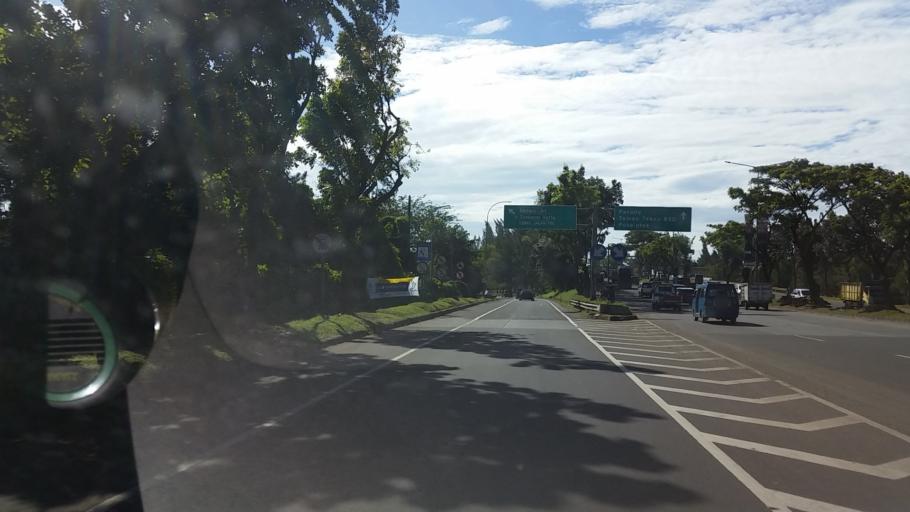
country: ID
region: West Java
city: Serpong
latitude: -6.3107
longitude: 106.6752
